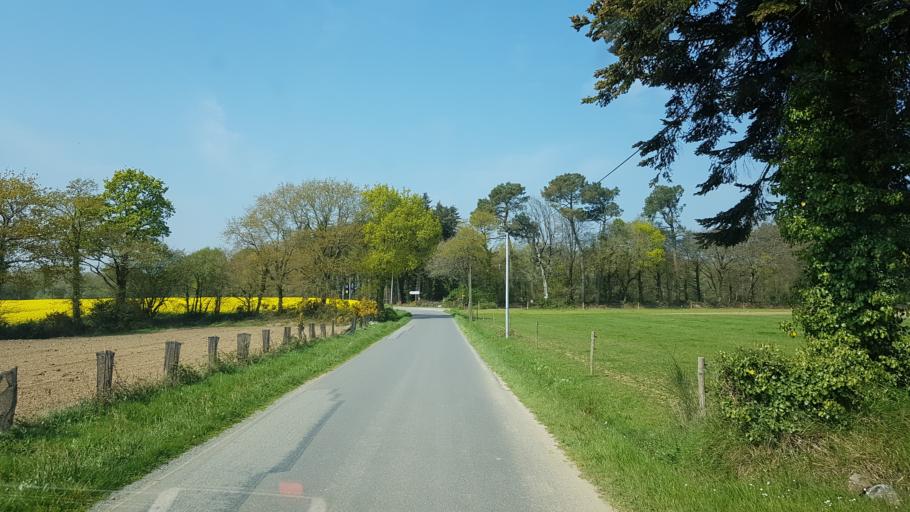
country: FR
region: Brittany
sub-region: Departement du Morbihan
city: Peaule
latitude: 47.5882
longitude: -2.3934
